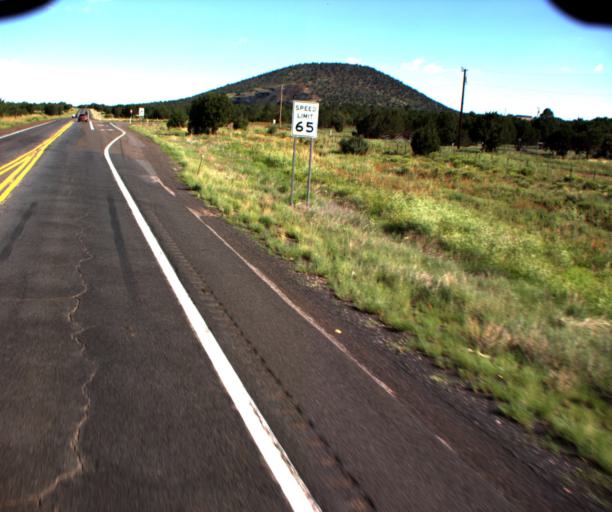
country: US
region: Arizona
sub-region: Coconino County
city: Williams
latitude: 35.3284
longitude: -112.1559
